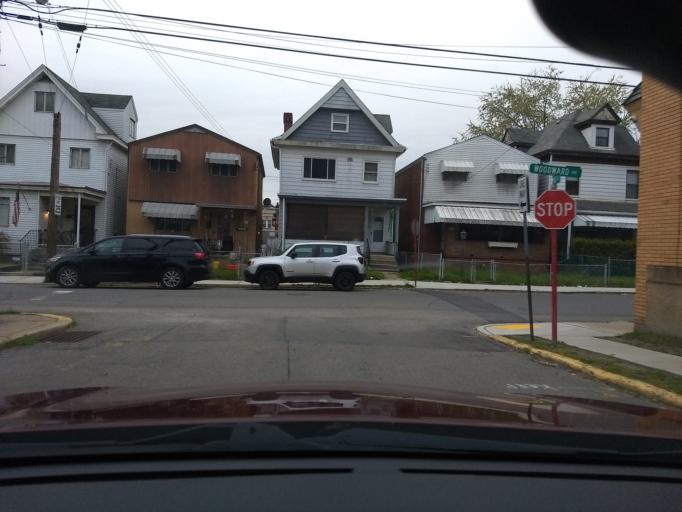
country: US
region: Pennsylvania
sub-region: Allegheny County
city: McKees Rocks
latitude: 40.4724
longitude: -80.0716
